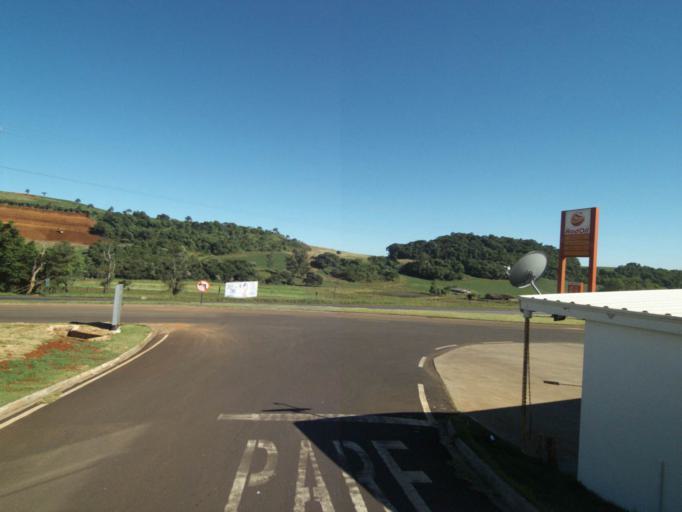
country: BR
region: Parana
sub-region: Pato Branco
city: Pato Branco
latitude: -26.2579
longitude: -52.7864
